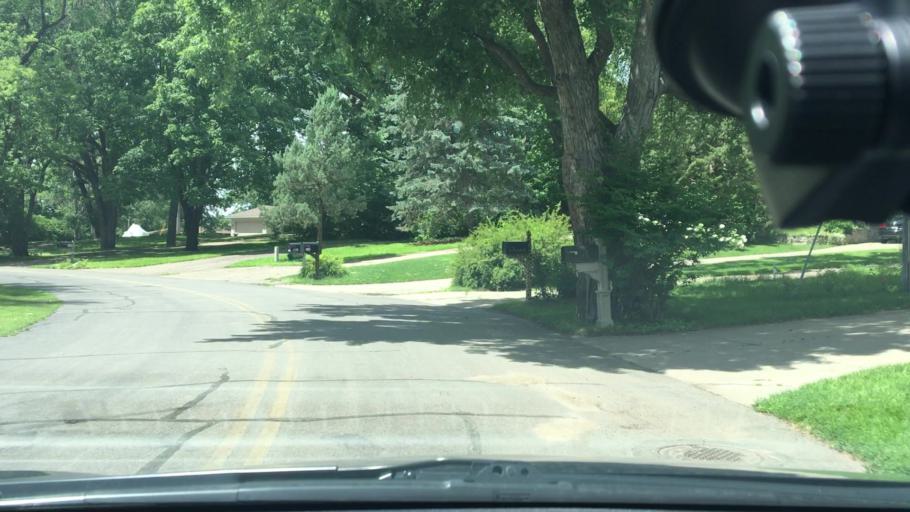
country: US
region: Minnesota
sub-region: Hennepin County
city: Plymouth
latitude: 45.0030
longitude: -93.4242
